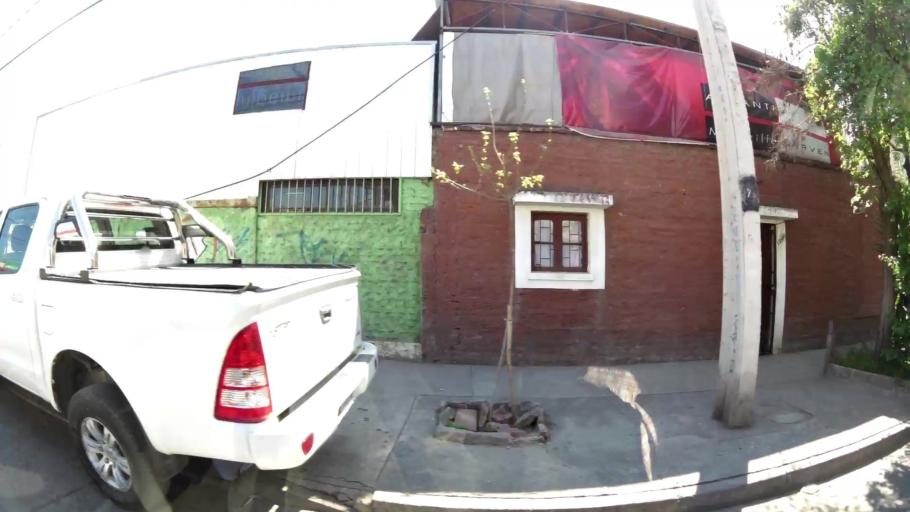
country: CL
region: Santiago Metropolitan
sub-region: Provincia de Santiago
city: Lo Prado
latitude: -33.4125
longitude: -70.6851
